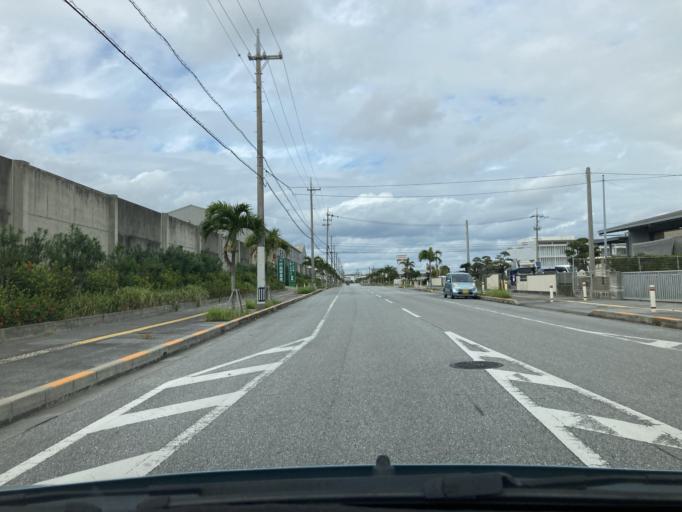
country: JP
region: Okinawa
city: Itoman
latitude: 26.1532
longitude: 127.6557
